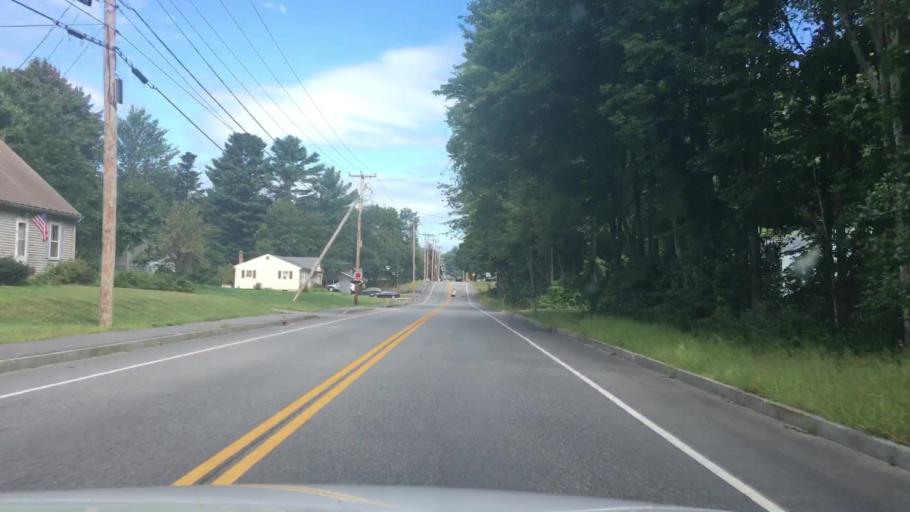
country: US
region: Maine
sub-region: Androscoggin County
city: Auburn
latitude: 44.1018
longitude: -70.2473
